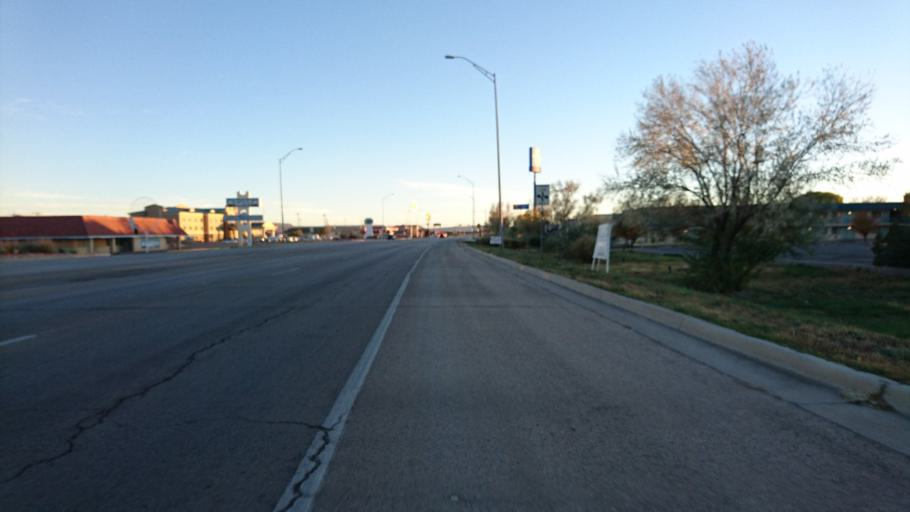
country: US
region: New Mexico
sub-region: Cibola County
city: Grants
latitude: 35.1312
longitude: -107.8274
